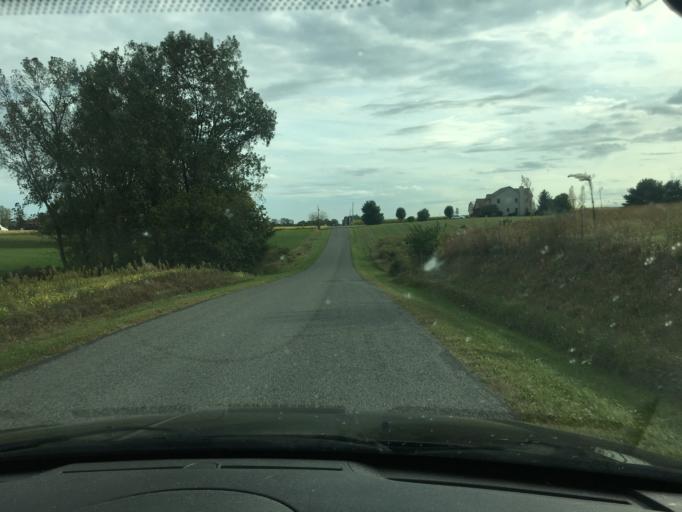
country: US
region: Ohio
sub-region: Logan County
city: Bellefontaine
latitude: 40.3243
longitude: -83.8059
